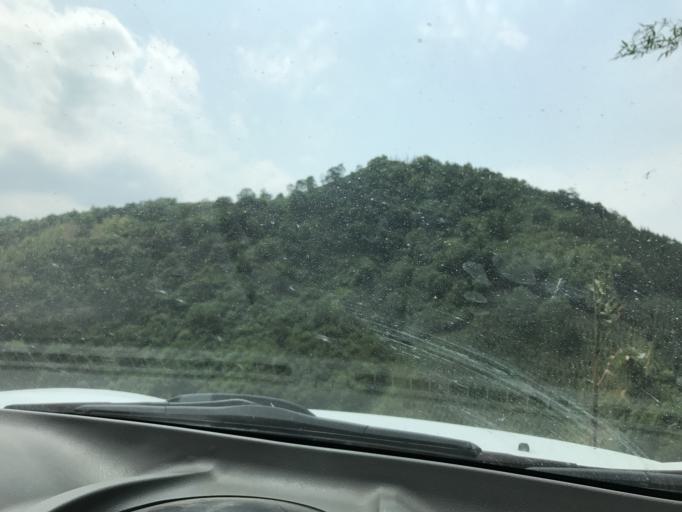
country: CN
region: Guangxi Zhuangzu Zizhiqu
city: Xinzhou
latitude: 24.9919
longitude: 105.9124
